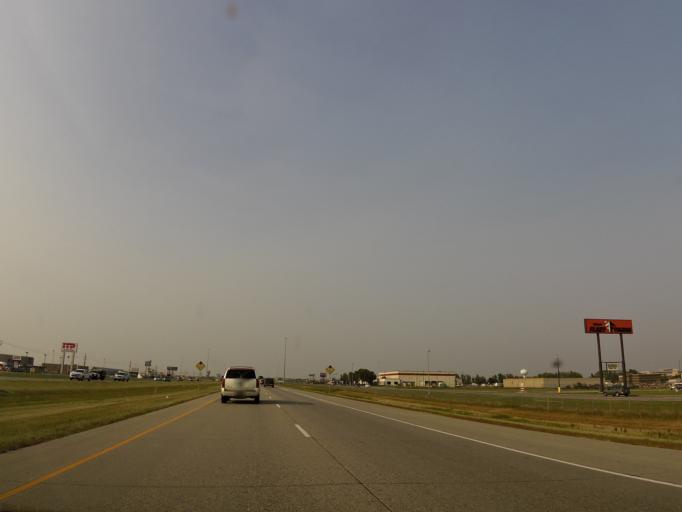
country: US
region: North Dakota
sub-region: Cass County
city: Fargo
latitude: 46.8226
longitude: -96.8395
